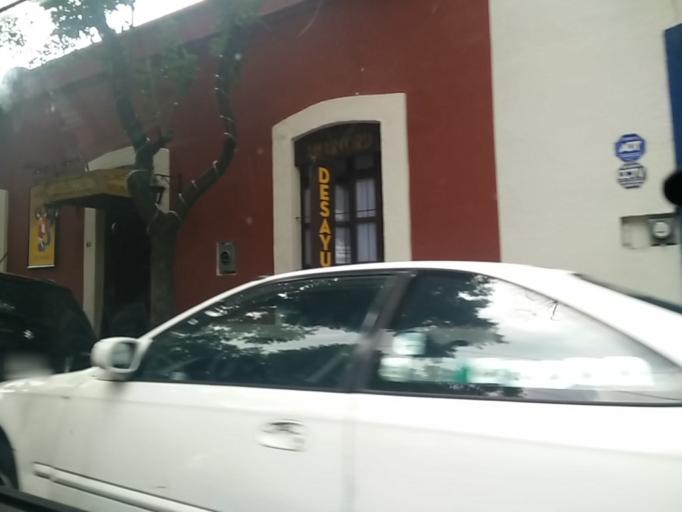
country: MX
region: Mexico City
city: Coyoacan
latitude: 19.3473
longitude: -99.1626
